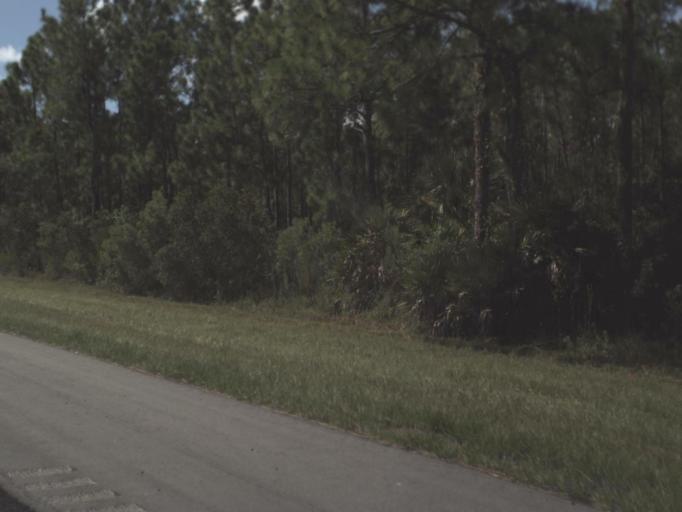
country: US
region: Florida
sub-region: Lee County
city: Suncoast Estates
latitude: 26.7630
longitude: -81.8752
